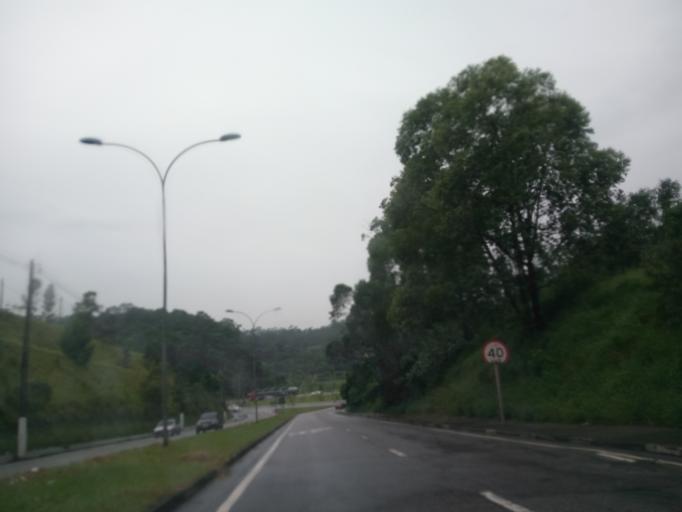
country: BR
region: Sao Paulo
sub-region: Sao Bernardo Do Campo
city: Sao Bernardo do Campo
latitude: -23.7594
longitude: -46.5882
